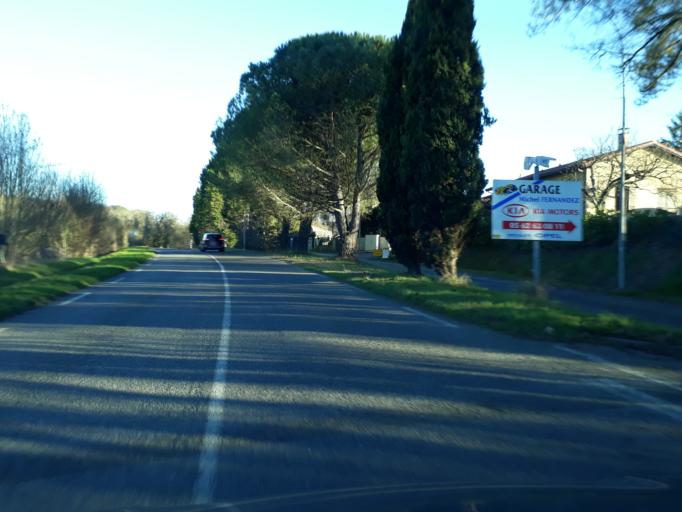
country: FR
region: Midi-Pyrenees
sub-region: Departement du Gers
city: Auch
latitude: 43.6362
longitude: 0.6055
